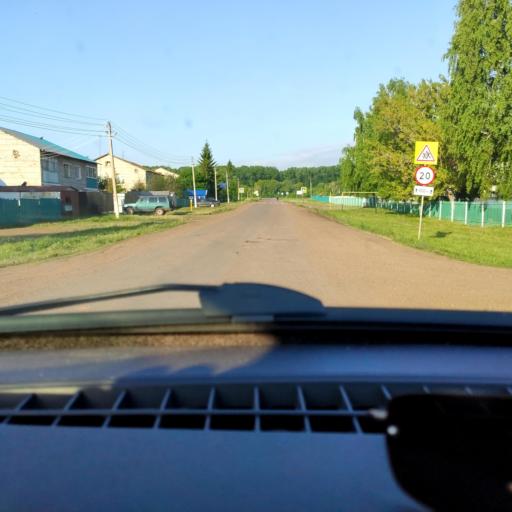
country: RU
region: Bashkortostan
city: Ulukulevo
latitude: 54.4686
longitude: 56.2322
